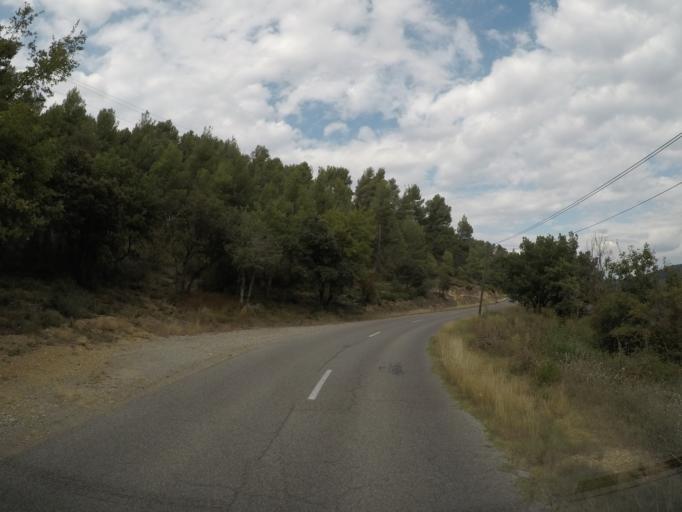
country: FR
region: Provence-Alpes-Cote d'Azur
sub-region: Departement des Alpes-de-Haute-Provence
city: Greoux-les-Bains
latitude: 43.7738
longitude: 5.9019
